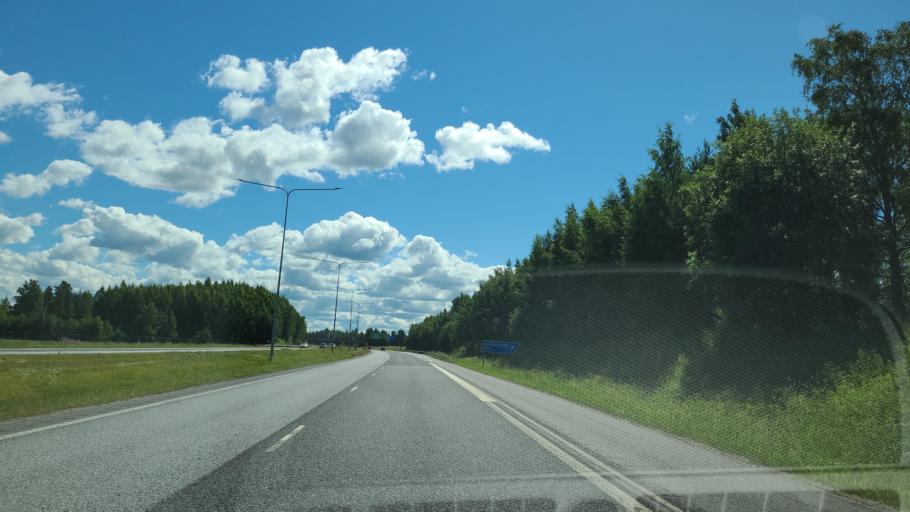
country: FI
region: Ostrobothnia
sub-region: Vaasa
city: Ristinummi
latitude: 63.0327
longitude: 21.7452
